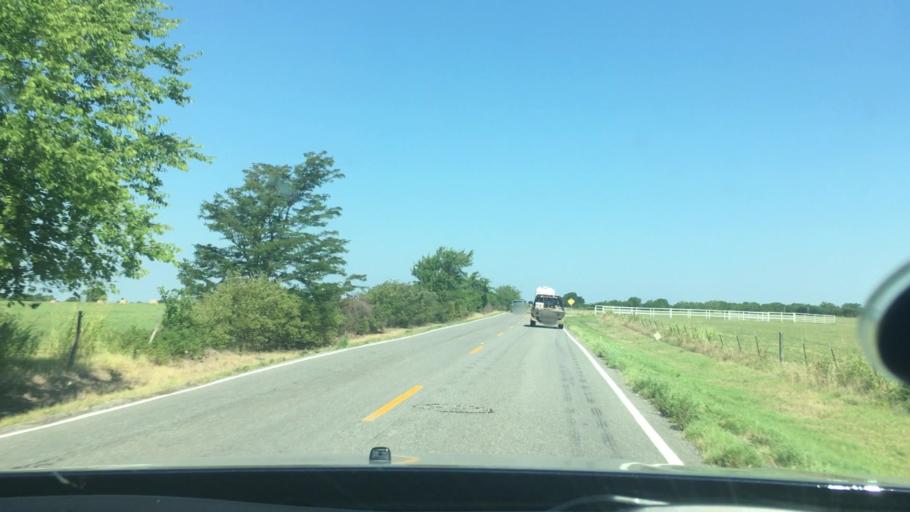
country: US
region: Oklahoma
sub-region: Johnston County
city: Tishomingo
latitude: 34.1956
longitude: -96.5380
